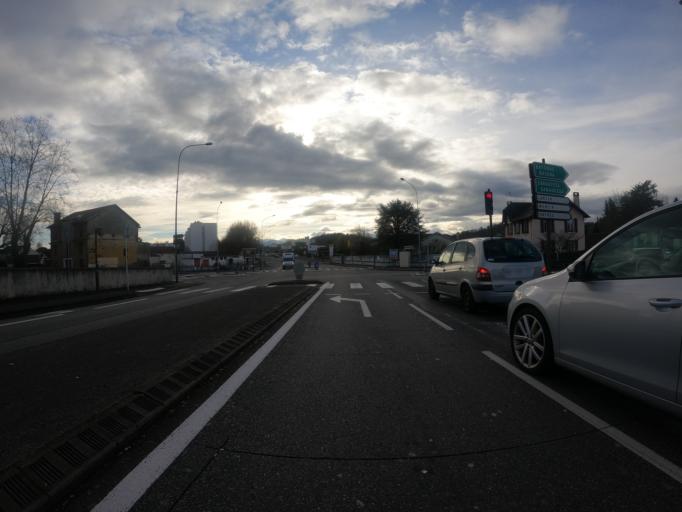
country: FR
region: Aquitaine
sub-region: Departement des Pyrenees-Atlantiques
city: Jurancon
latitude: 43.2932
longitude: -0.3867
